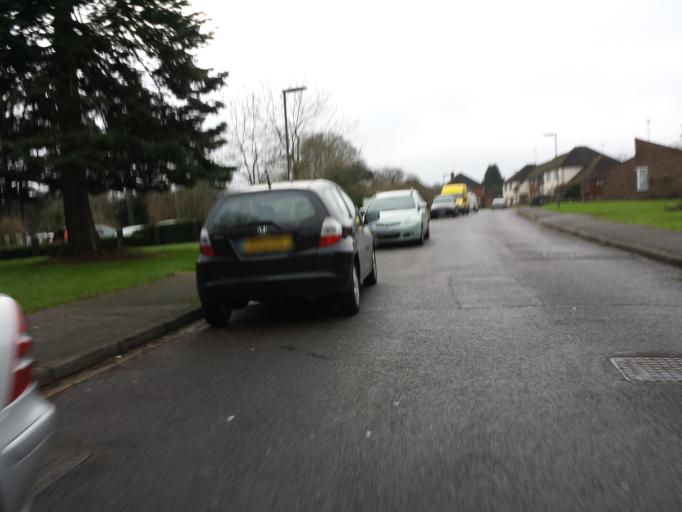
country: GB
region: England
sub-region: Surrey
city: Bagshot
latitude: 51.3592
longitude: -0.6850
